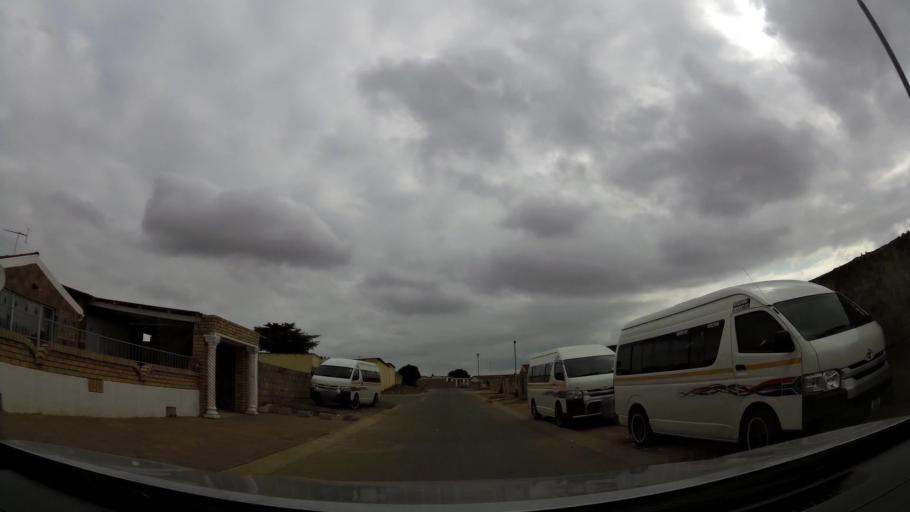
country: ZA
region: Eastern Cape
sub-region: Nelson Mandela Bay Metropolitan Municipality
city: Port Elizabeth
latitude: -33.8760
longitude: 25.5636
